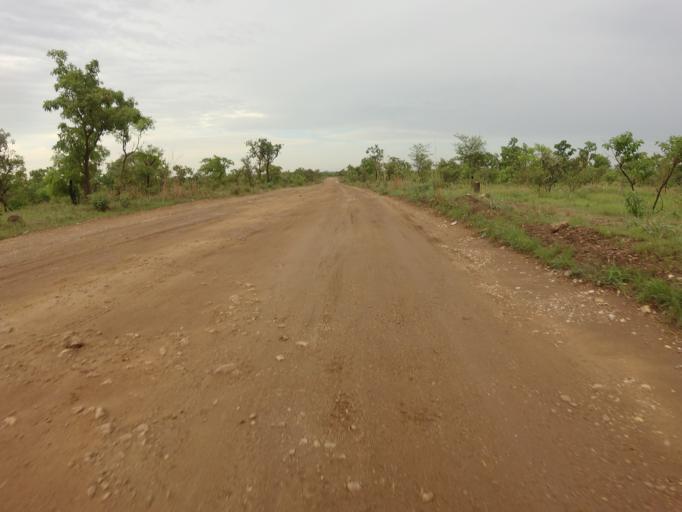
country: GH
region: Upper East
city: Bolgatanga
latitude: 10.8788
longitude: -0.6227
